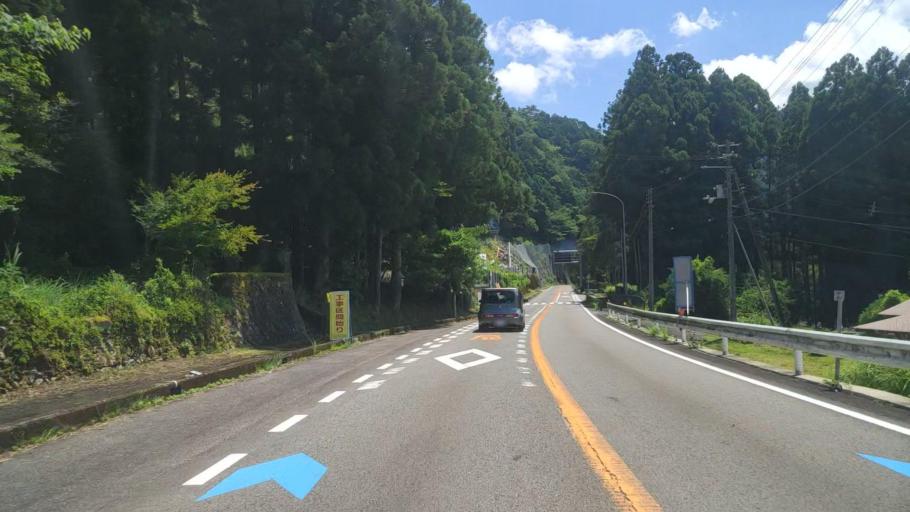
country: JP
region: Mie
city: Owase
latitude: 33.9832
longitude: 136.1081
